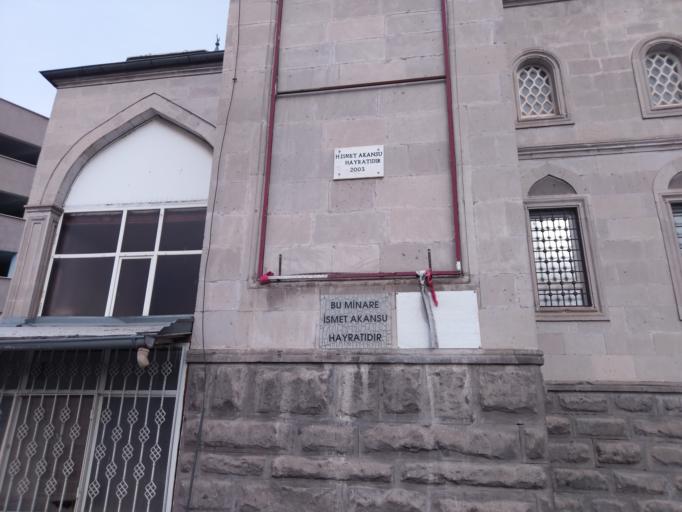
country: TR
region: Kayseri
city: Kayseri
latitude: 38.7151
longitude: 35.4916
